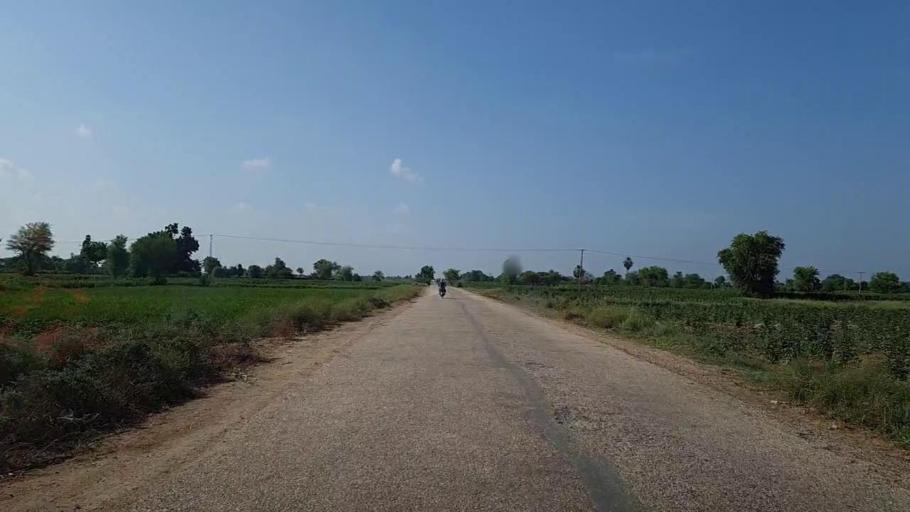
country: PK
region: Sindh
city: Kandiaro
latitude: 27.0566
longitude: 68.3172
